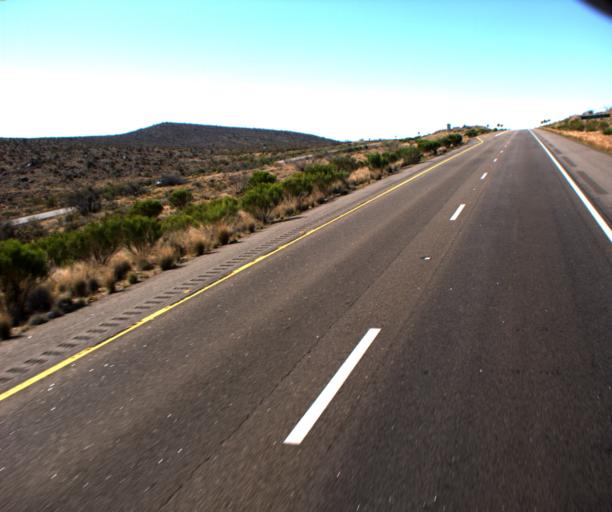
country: US
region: Arizona
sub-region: Mohave County
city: Kingman
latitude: 34.9589
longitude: -113.6700
